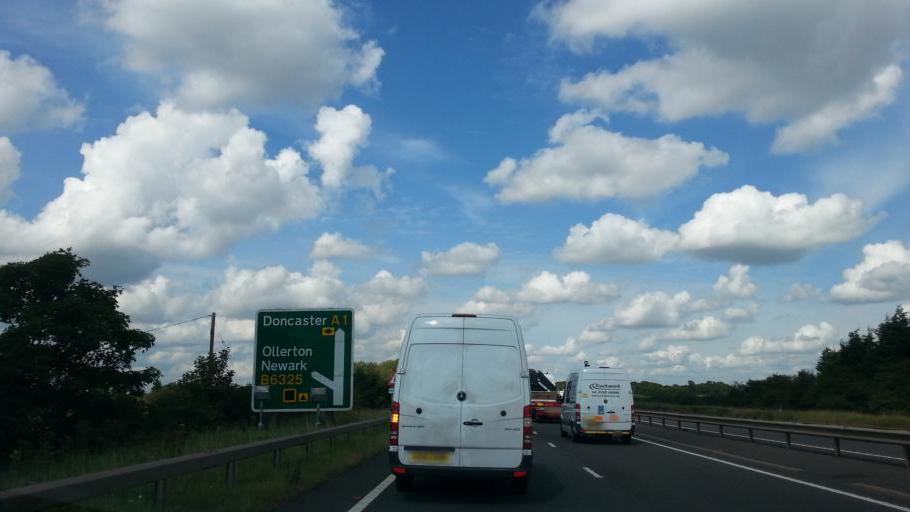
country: GB
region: England
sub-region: Nottinghamshire
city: Newark on Trent
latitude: 53.1145
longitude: -0.8158
